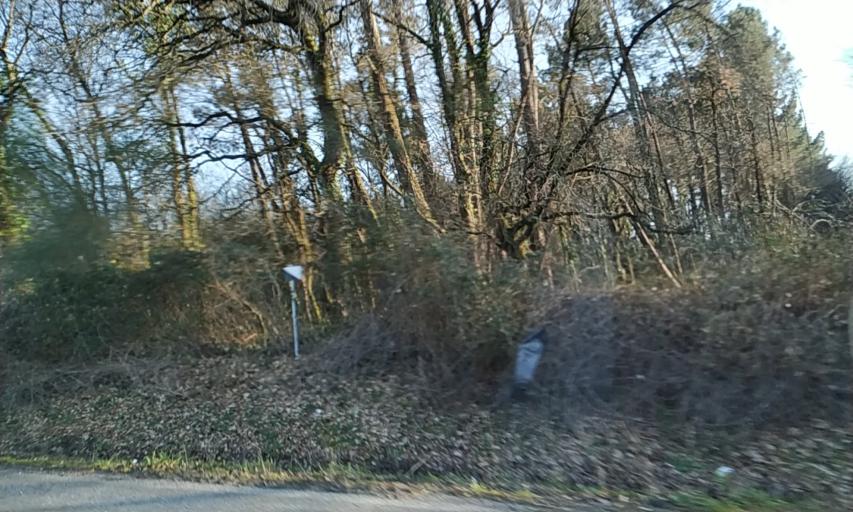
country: ES
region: Galicia
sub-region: Provincia de Lugo
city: Corgo
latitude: 42.9364
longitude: -7.4096
